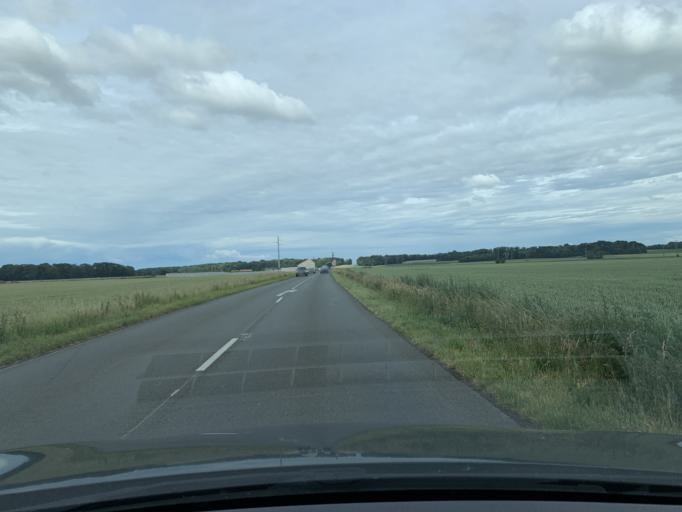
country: FR
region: Nord-Pas-de-Calais
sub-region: Departement du Nord
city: Cantin
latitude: 50.3182
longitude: 3.1366
